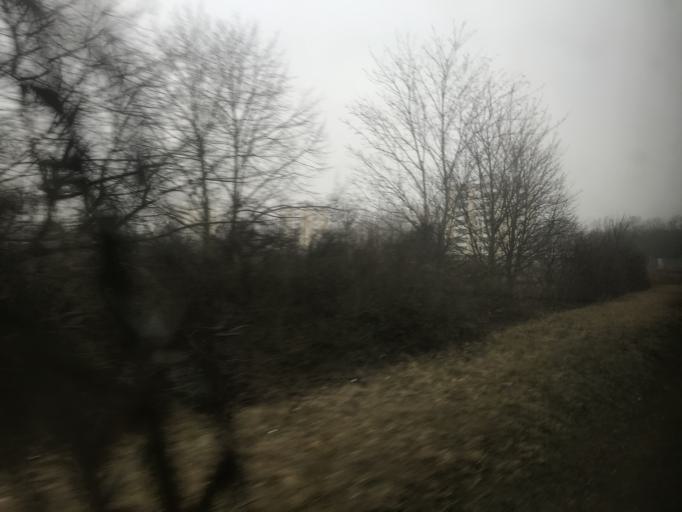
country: DE
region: Rheinland-Pfalz
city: Frankenthal
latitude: 49.5203
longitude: 8.3494
